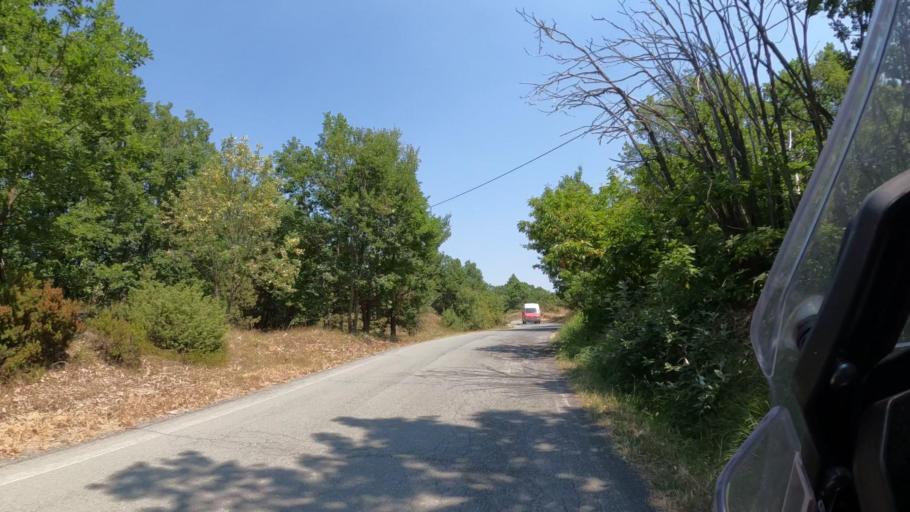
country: IT
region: Piedmont
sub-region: Provincia di Alessandria
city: Morbello
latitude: 44.5746
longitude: 8.5269
